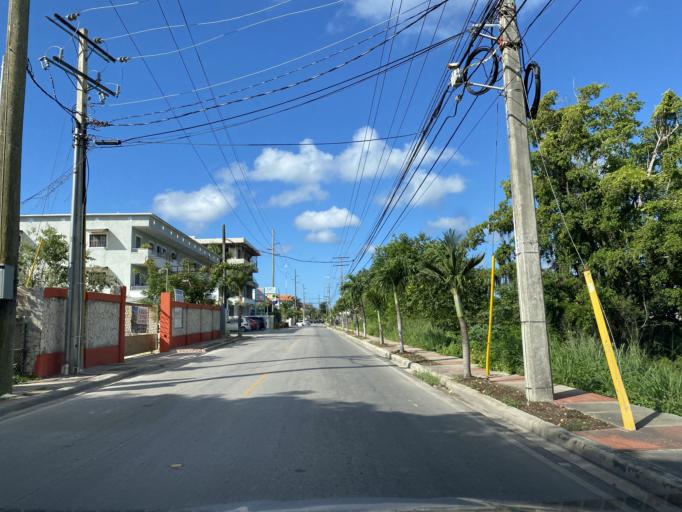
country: DO
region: La Romana
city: La Romana
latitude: 18.3703
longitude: -68.8347
